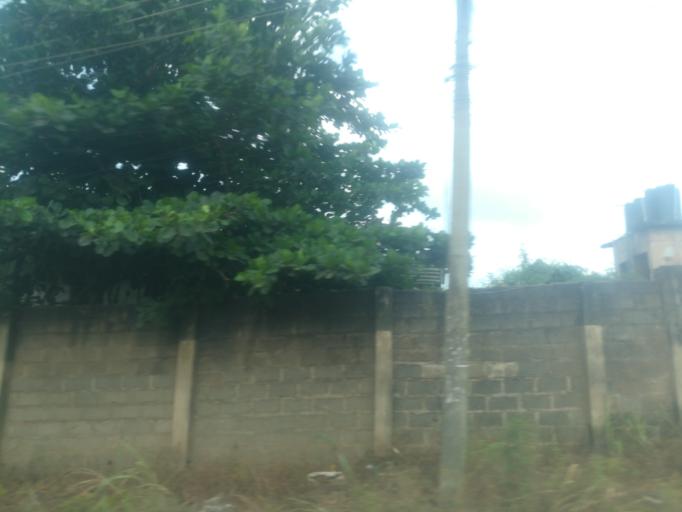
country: NG
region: Ogun
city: Abeokuta
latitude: 7.1249
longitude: 3.3217
